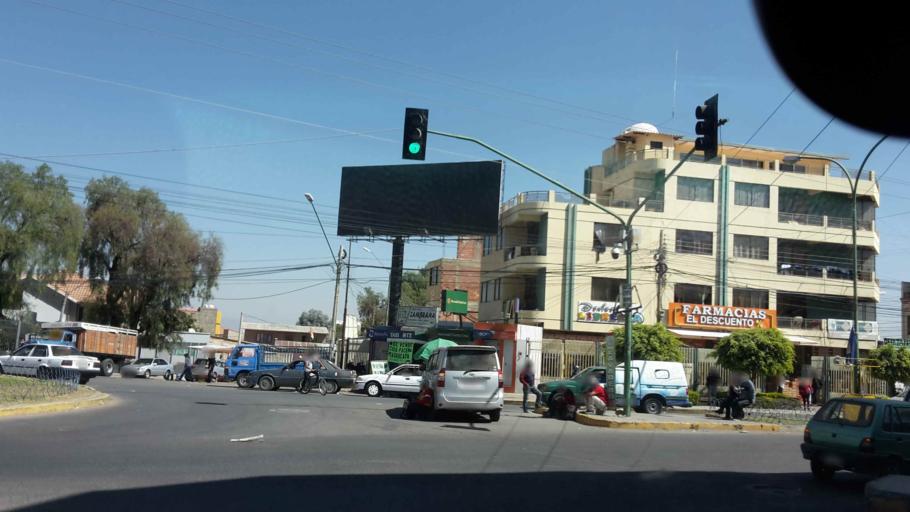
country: BO
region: Cochabamba
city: Cochabamba
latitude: -17.3547
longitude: -66.1880
